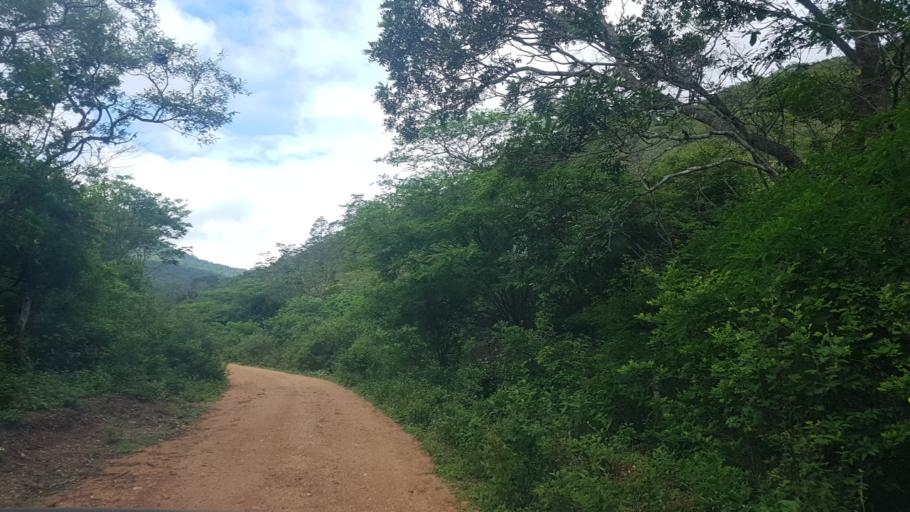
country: NI
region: Nueva Segovia
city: Ocotal
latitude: 13.6346
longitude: -86.6072
